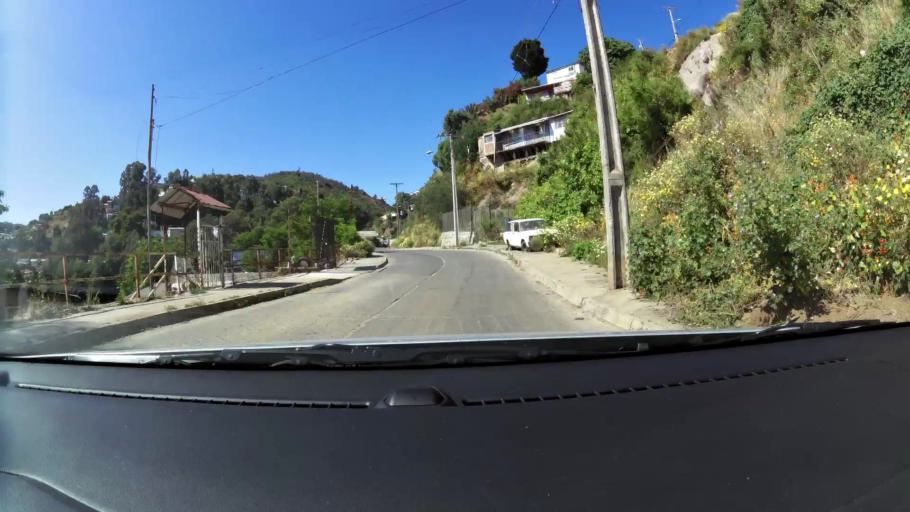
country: CL
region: Valparaiso
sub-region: Provincia de Valparaiso
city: Valparaiso
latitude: -33.0667
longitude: -71.5899
